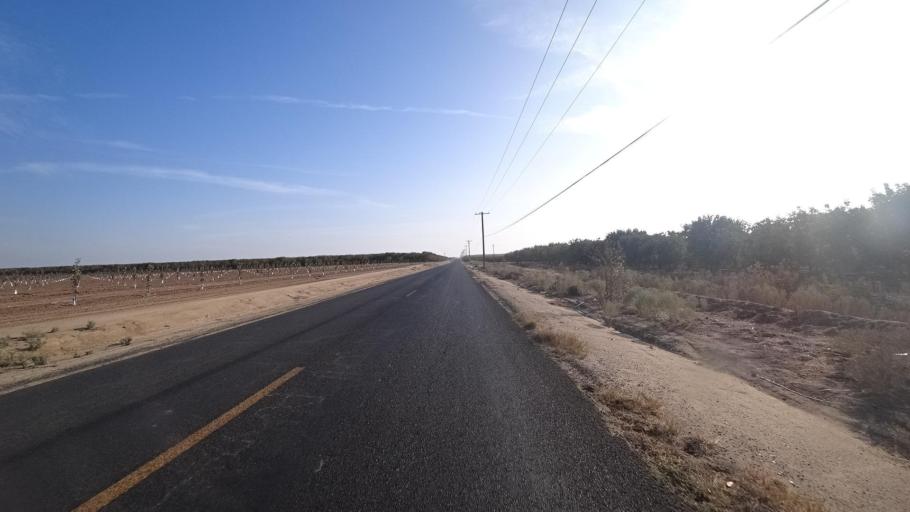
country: US
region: California
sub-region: Kern County
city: McFarland
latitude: 35.6746
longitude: -119.1670
